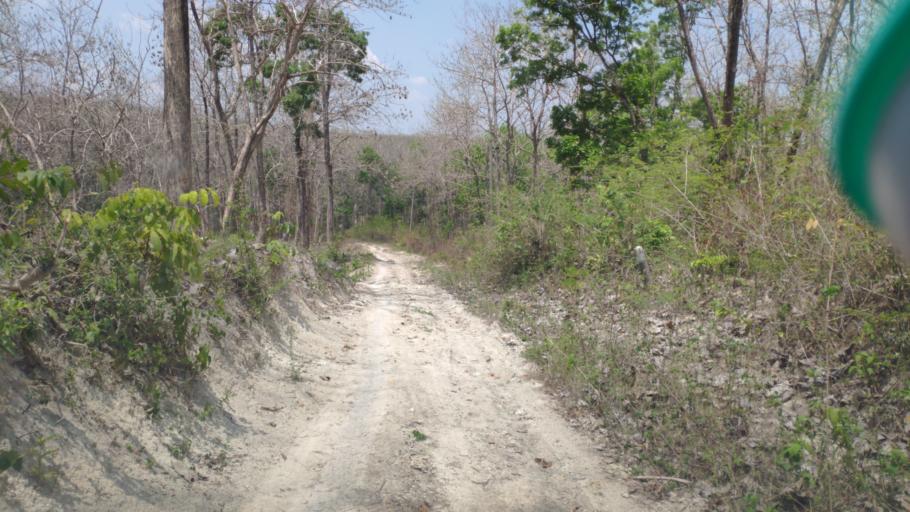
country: ID
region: Central Java
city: Randublatung
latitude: -7.2646
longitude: 111.3315
